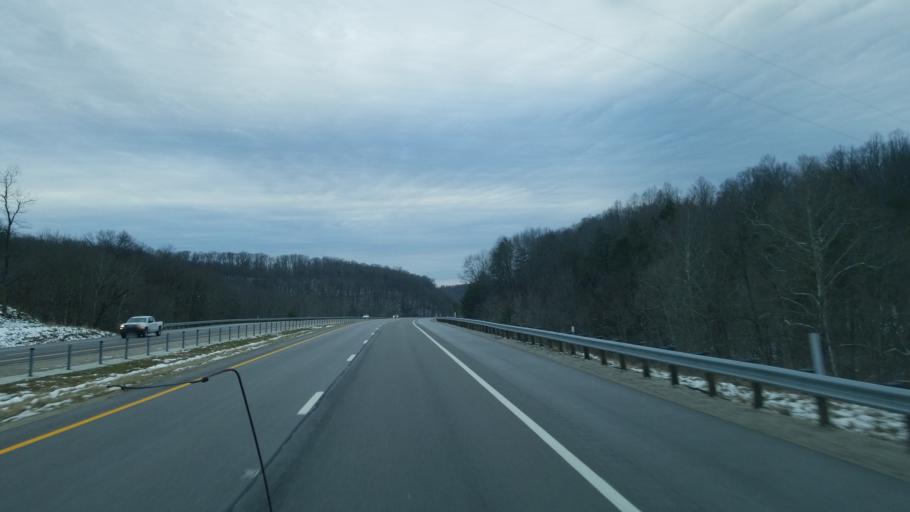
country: US
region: West Virginia
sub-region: Jackson County
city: Ravenswood
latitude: 38.9664
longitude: -81.6954
